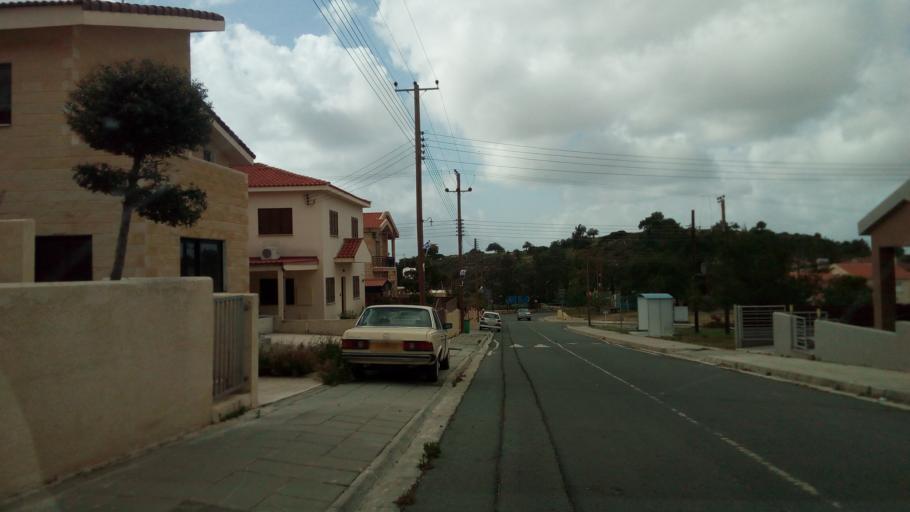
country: CY
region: Limassol
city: Sotira
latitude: 34.7123
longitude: 32.8634
